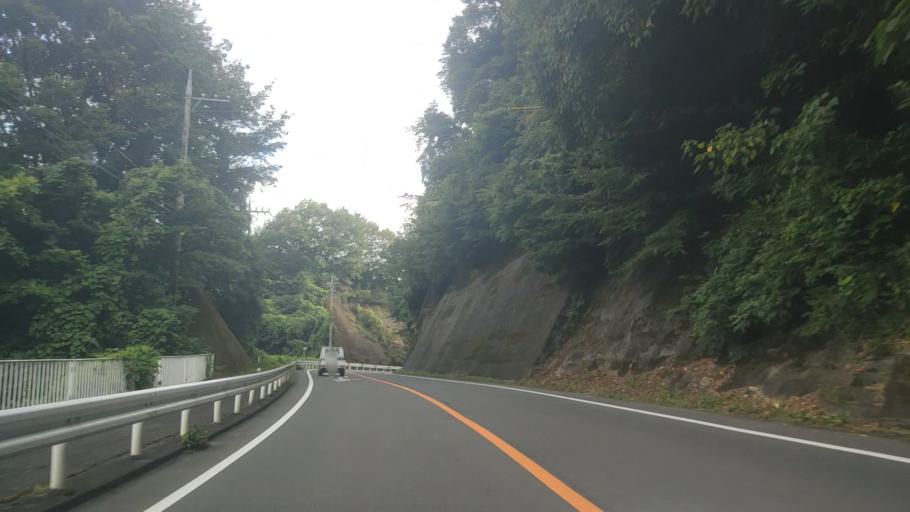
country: JP
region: Gunma
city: Omamacho-omama
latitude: 36.5480
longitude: 139.3720
